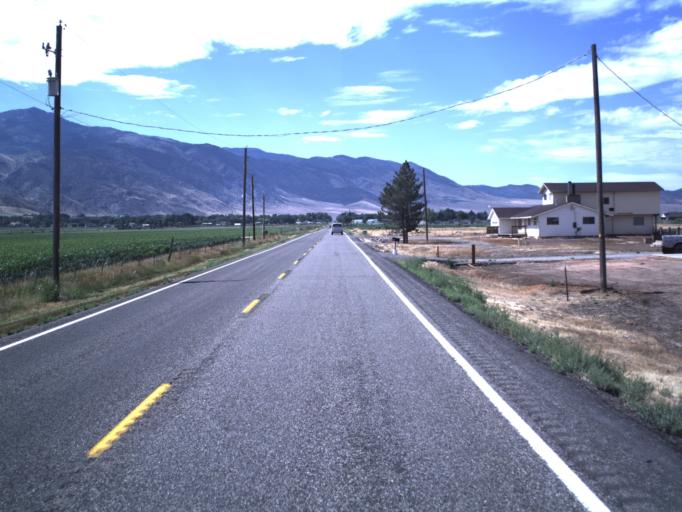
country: US
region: Utah
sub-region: Sevier County
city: Monroe
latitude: 38.6569
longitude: -112.1215
